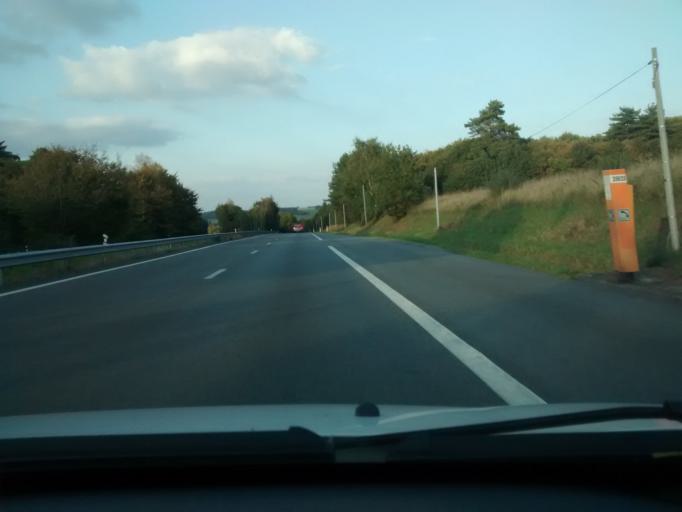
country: FR
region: Brittany
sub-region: Departement d'Ille-et-Vilaine
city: La Dominelais
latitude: 47.7920
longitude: -1.6929
